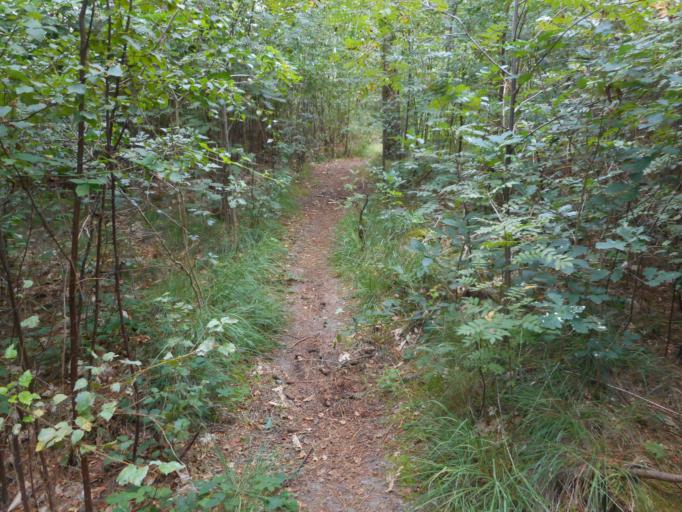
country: BE
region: Flanders
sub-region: Provincie Antwerpen
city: Vorselaar
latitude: 51.2483
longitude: 4.7722
